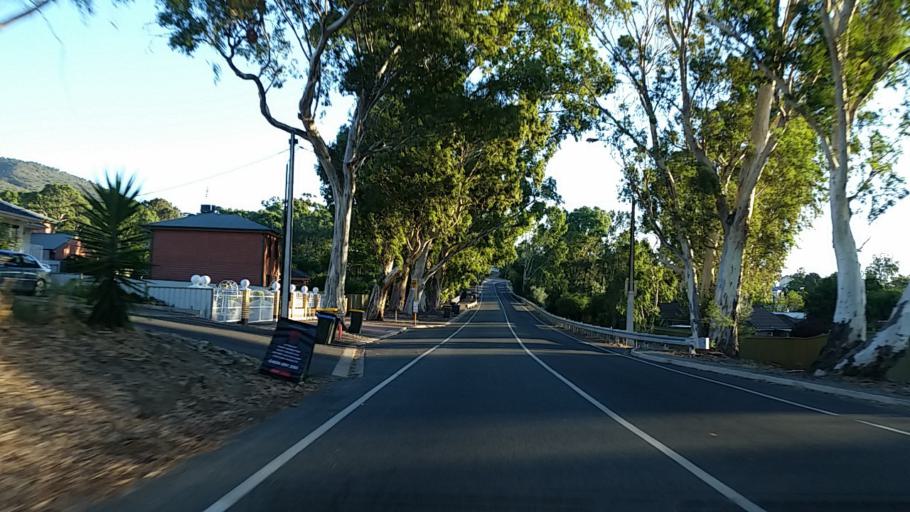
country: AU
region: South Australia
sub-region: Campbelltown
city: Athelstone
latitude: -34.8658
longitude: 138.7087
